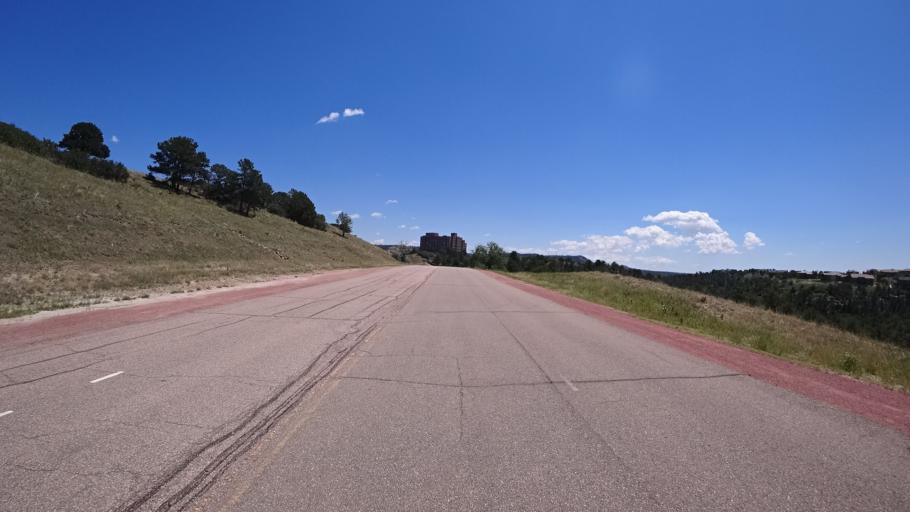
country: US
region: Colorado
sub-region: El Paso County
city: Colorado Springs
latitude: 38.9143
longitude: -104.8348
